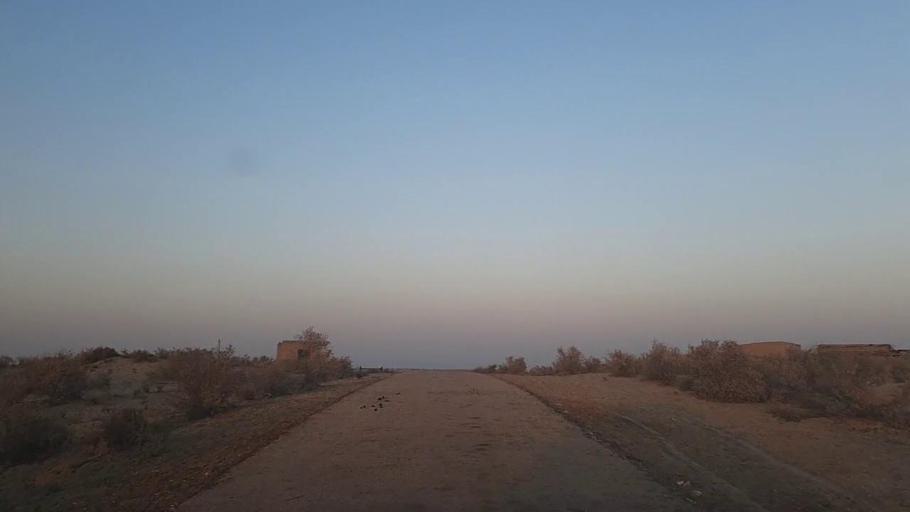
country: PK
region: Sindh
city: Jam Sahib
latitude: 26.3852
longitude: 68.6942
